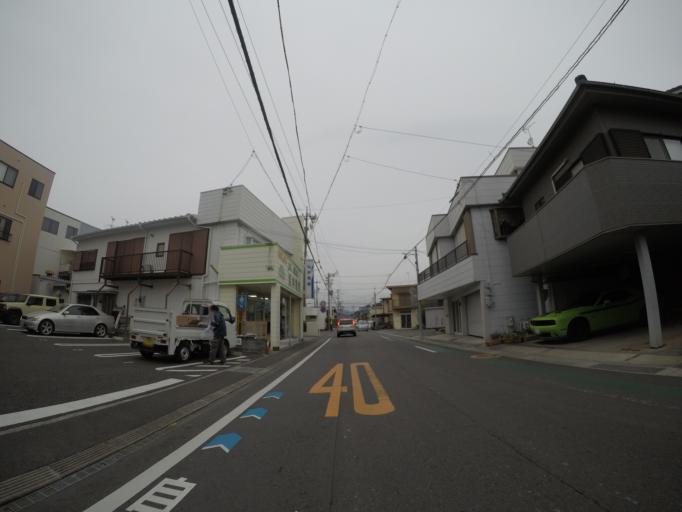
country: JP
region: Shizuoka
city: Shizuoka-shi
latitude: 34.9988
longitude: 138.4166
